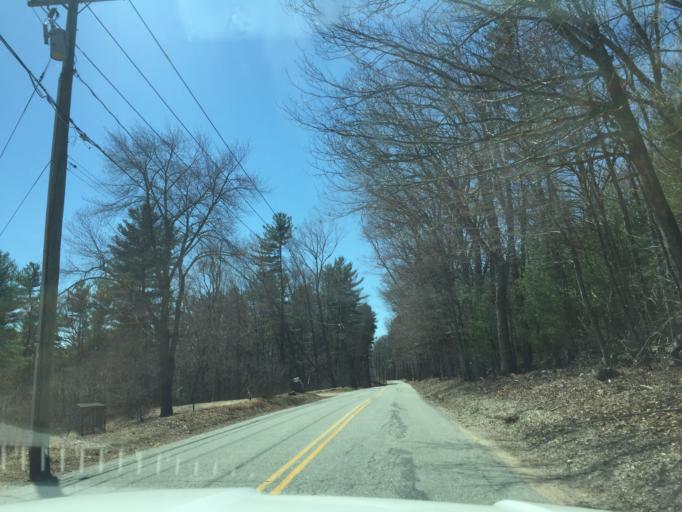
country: US
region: Connecticut
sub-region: Windham County
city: Quinebaug
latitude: 41.9998
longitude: -71.9510
